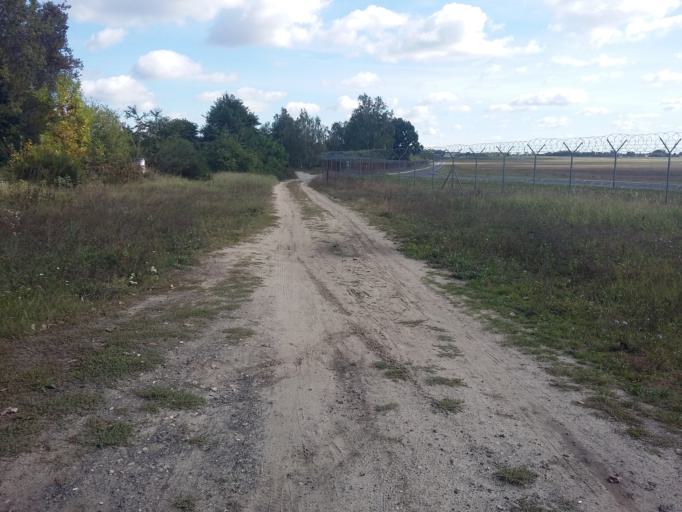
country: PL
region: Lodz Voivodeship
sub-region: Powiat pabianicki
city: Ksawerow
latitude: 51.7216
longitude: 19.3856
